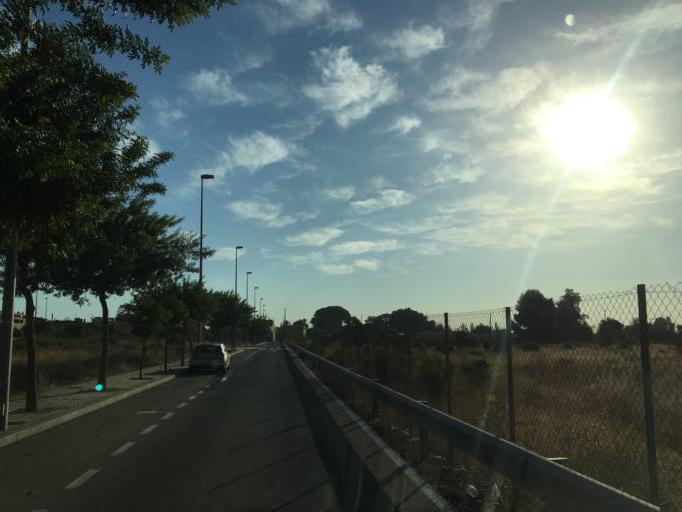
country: ES
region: Murcia
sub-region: Murcia
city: Murcia
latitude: 38.0151
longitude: -1.1475
